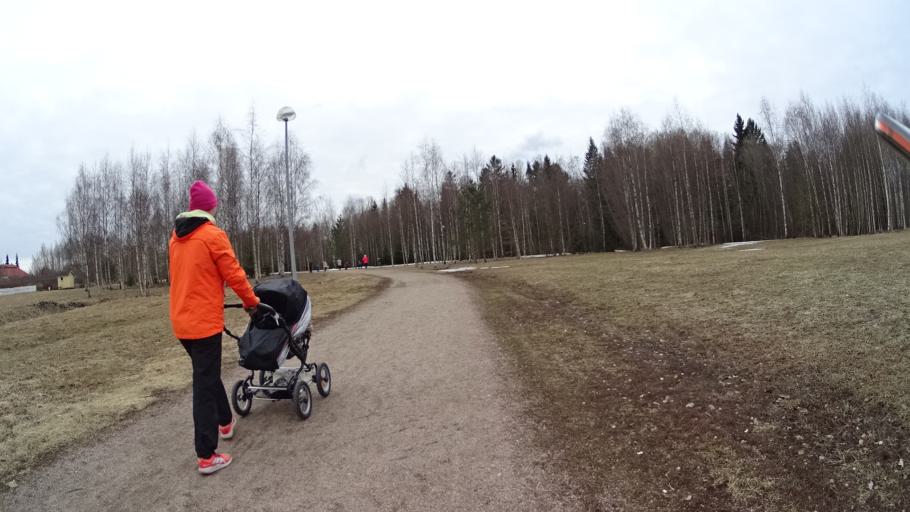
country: FI
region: Uusimaa
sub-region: Helsinki
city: Vantaa
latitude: 60.2884
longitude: 24.9394
